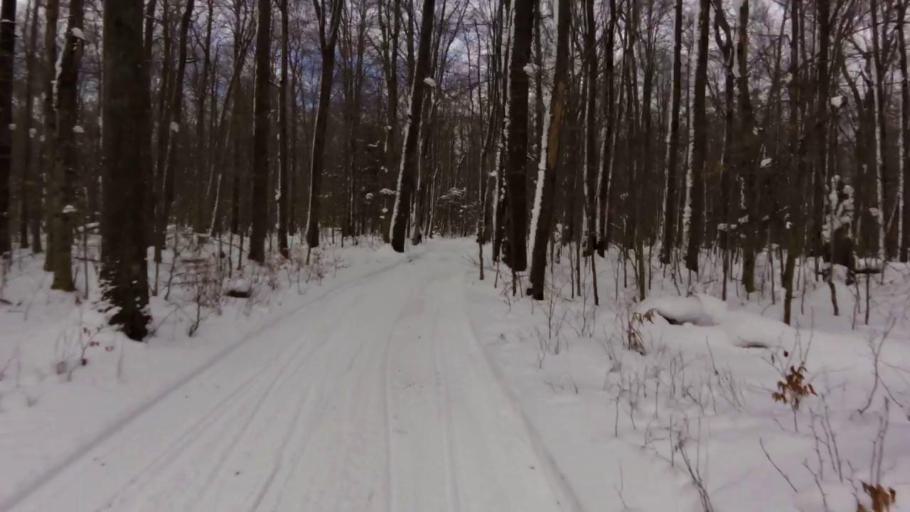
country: US
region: New York
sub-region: Cattaraugus County
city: Salamanca
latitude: 42.0417
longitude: -78.7552
